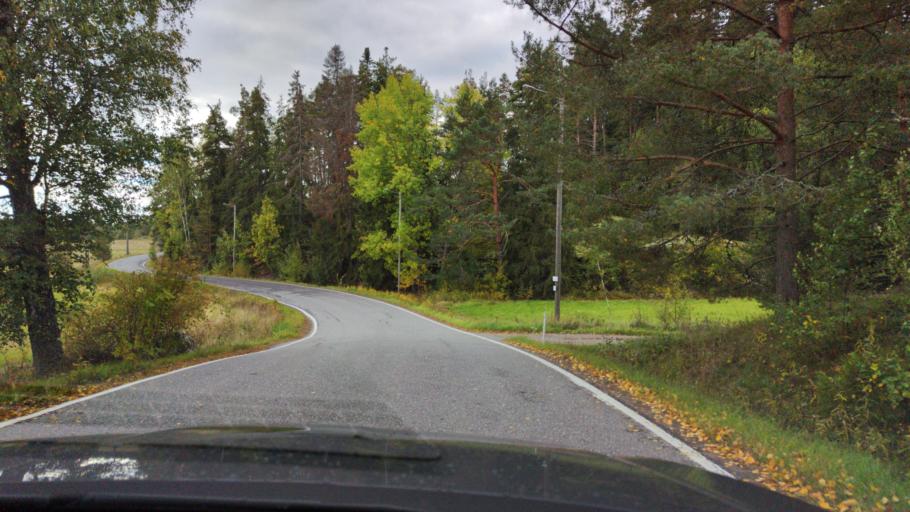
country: FI
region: Varsinais-Suomi
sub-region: Aboland-Turunmaa
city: Pargas
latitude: 60.3688
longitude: 22.2757
